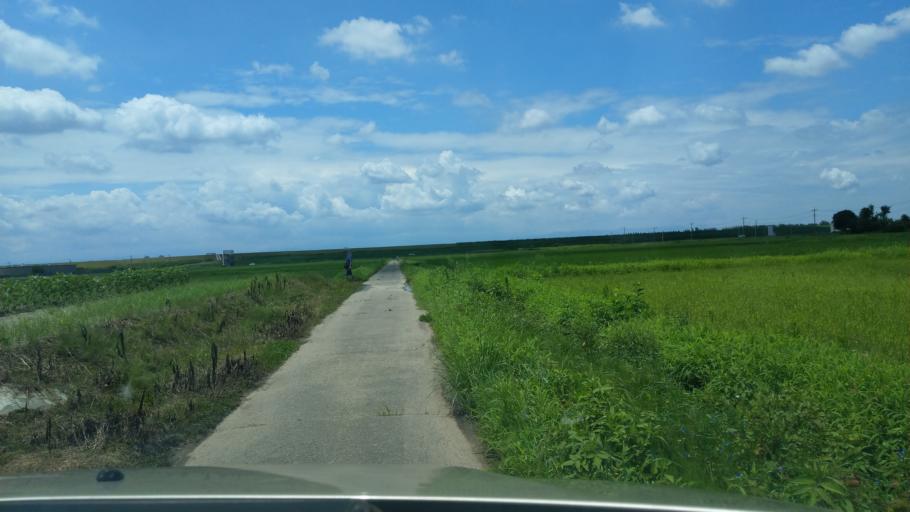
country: JP
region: Saitama
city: Yono
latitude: 35.8811
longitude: 139.5869
